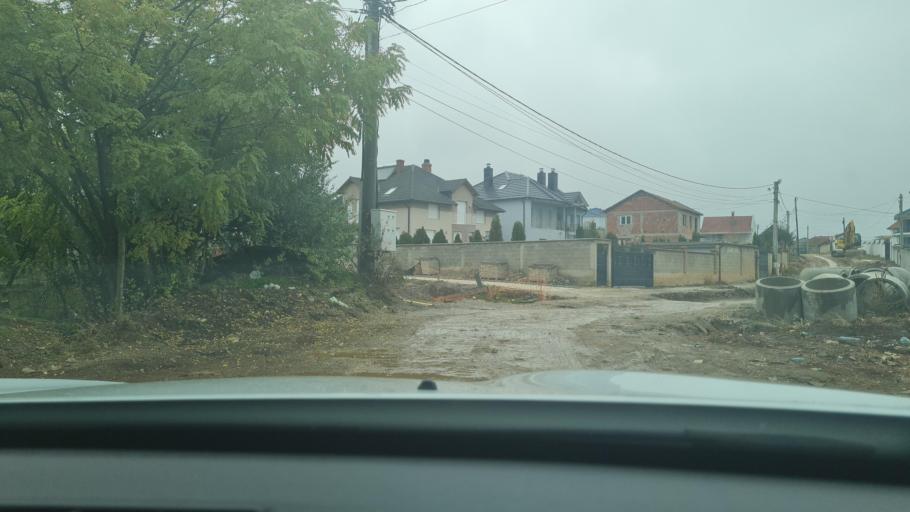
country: MK
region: Opstina Lipkovo
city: Matejche
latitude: 42.1205
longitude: 21.6025
